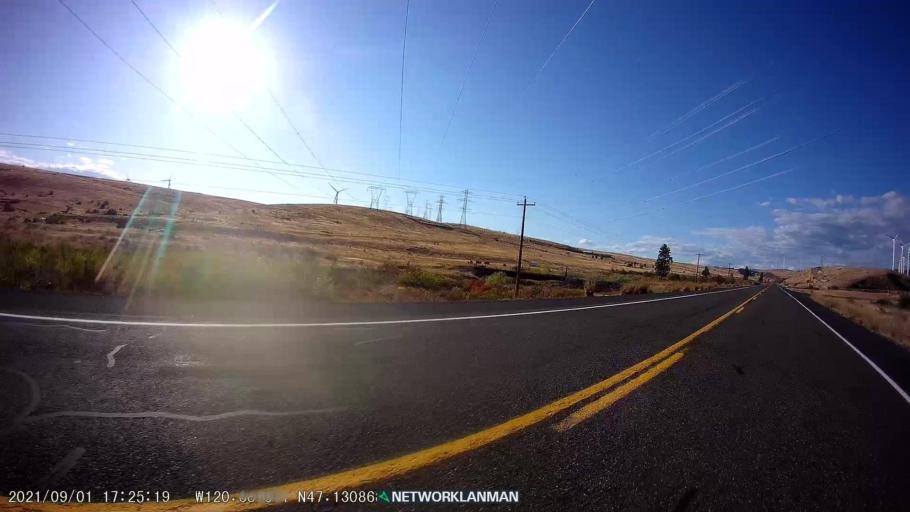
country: US
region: Washington
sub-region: Kittitas County
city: Ellensburg
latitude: 47.1310
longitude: -120.6854
